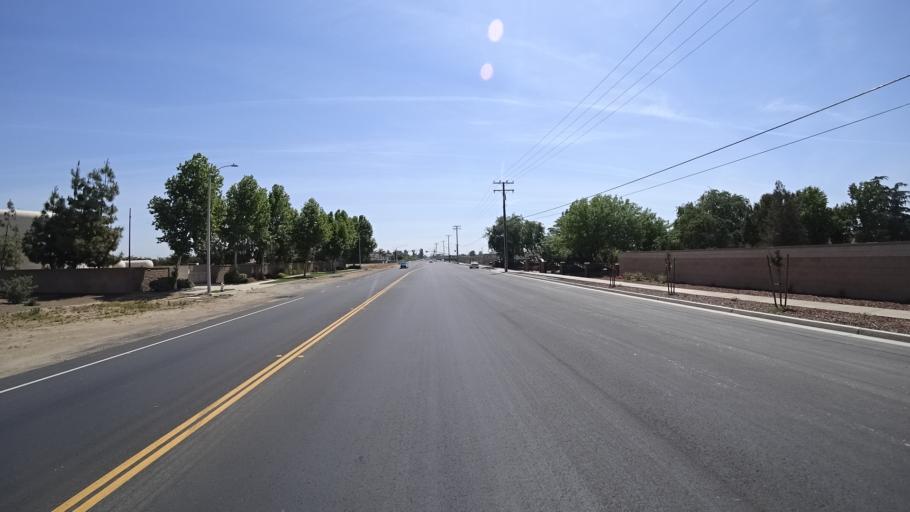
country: US
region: California
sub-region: Kings County
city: Armona
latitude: 36.3426
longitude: -119.6845
